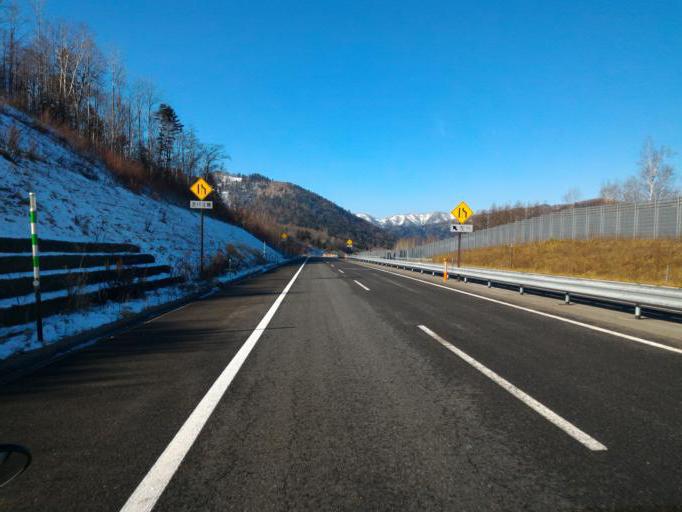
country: JP
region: Hokkaido
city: Shimo-furano
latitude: 43.0544
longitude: 142.5733
